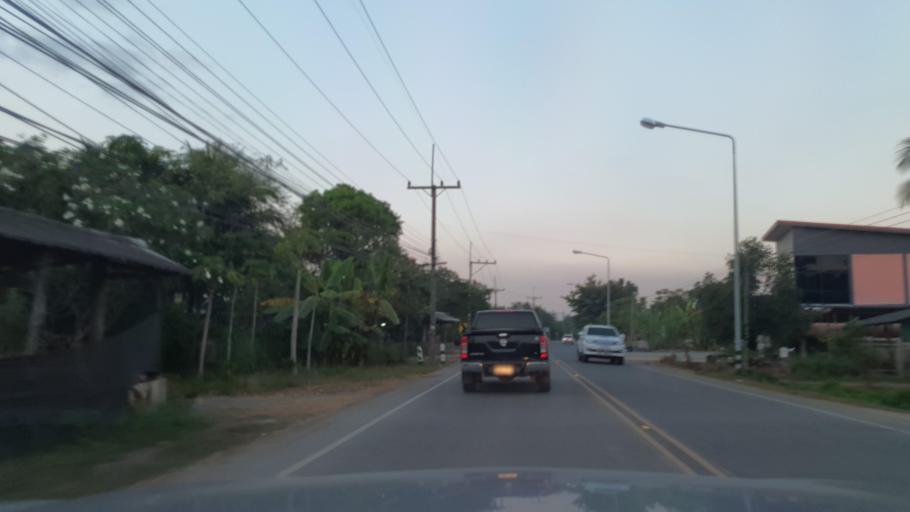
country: TH
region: Phayao
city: Dok Kham Tai
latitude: 19.0842
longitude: 100.0629
